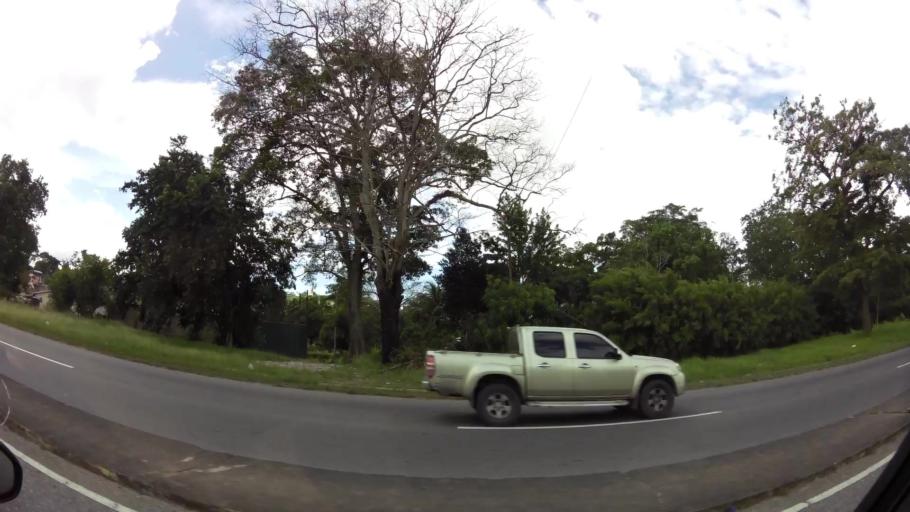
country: TT
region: City of San Fernando
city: Mon Repos
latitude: 10.2836
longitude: -61.4479
